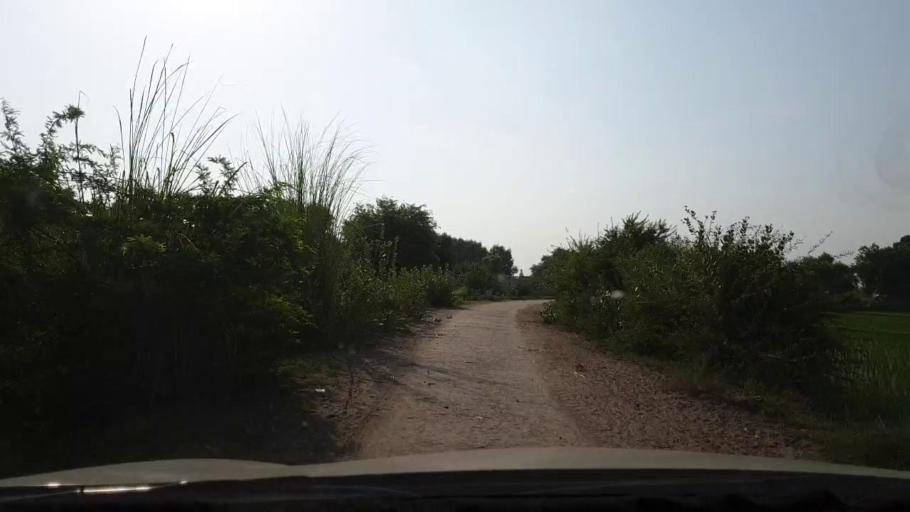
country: PK
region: Sindh
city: Larkana
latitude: 27.5506
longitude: 68.2655
